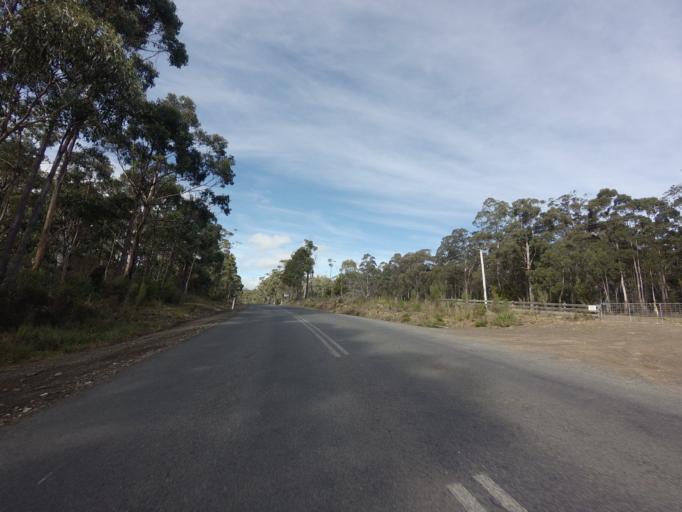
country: AU
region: Tasmania
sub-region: Clarence
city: Sandford
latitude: -43.1235
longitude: 147.7655
